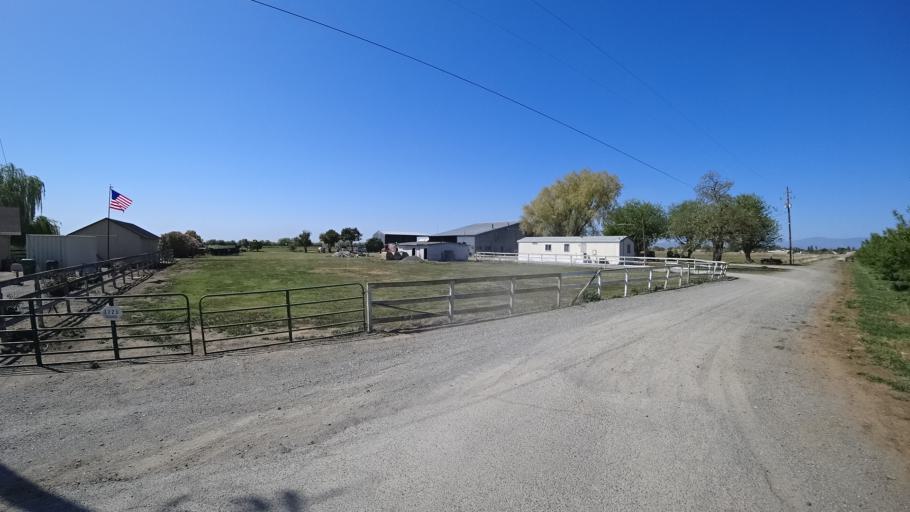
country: US
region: California
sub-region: Glenn County
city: Willows
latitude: 39.5145
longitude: -122.1865
